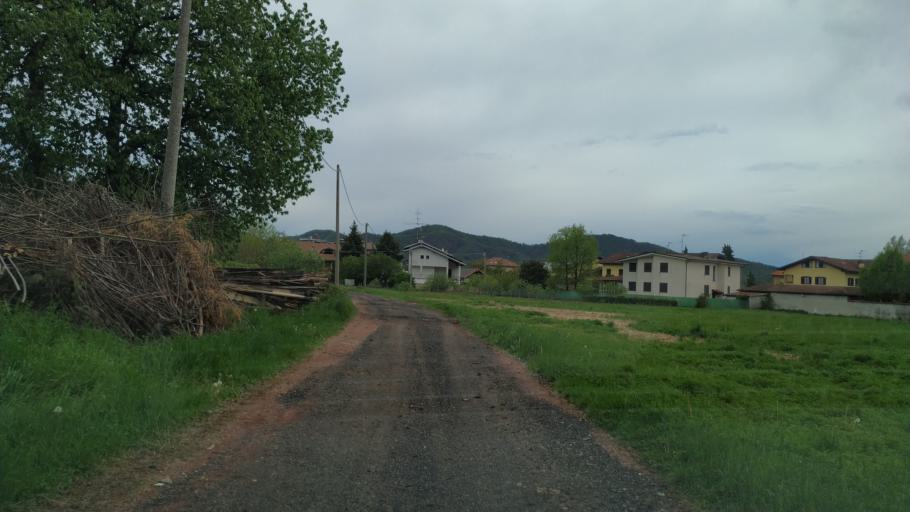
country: IT
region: Piedmont
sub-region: Provincia di Novara
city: Grignasco
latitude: 45.6763
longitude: 8.3467
